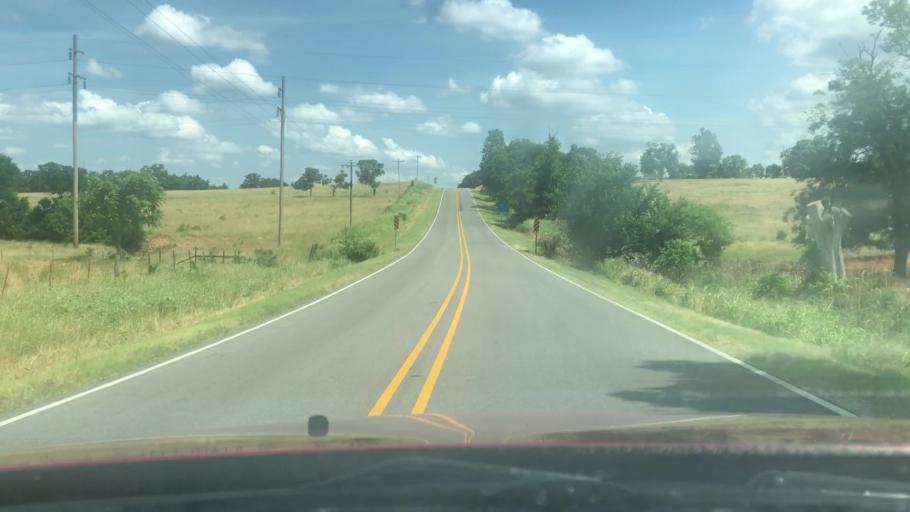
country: US
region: Arkansas
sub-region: Carroll County
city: Berryville
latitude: 36.3938
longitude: -93.5479
